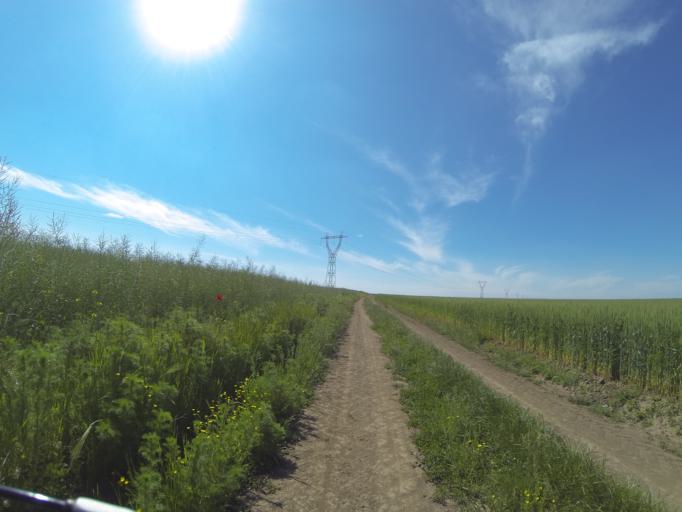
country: RO
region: Dolj
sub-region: Comuna Cosoveni
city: Cosoveni
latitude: 44.2580
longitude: 24.0040
